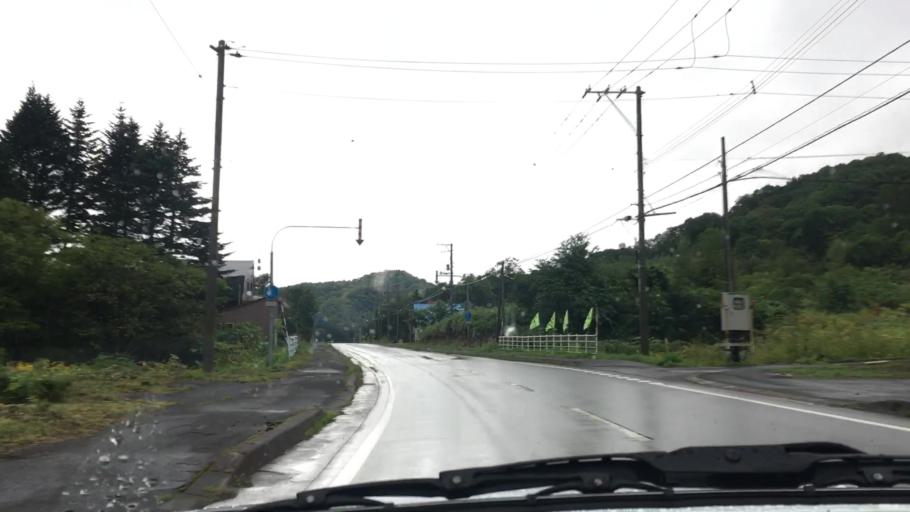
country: JP
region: Hokkaido
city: Niseko Town
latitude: 42.6451
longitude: 140.7331
